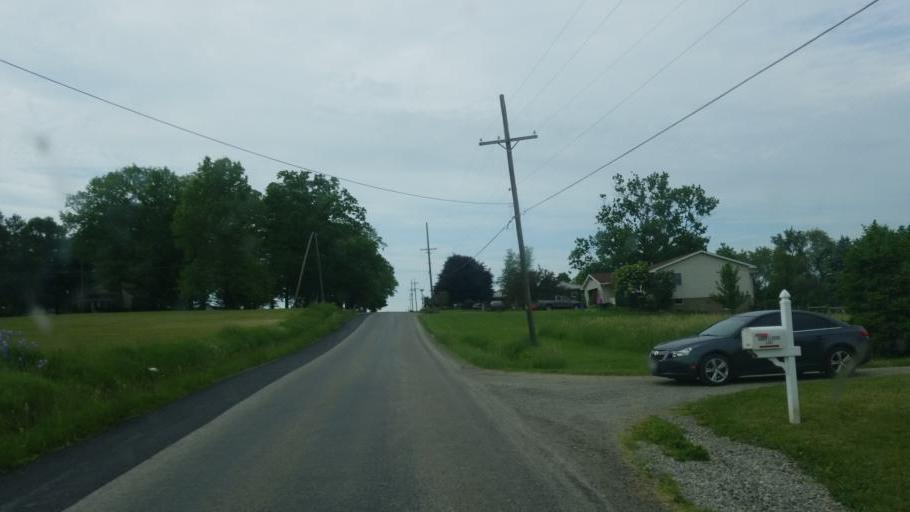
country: US
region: Ohio
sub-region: Wayne County
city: Dalton
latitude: 40.7789
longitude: -81.7551
